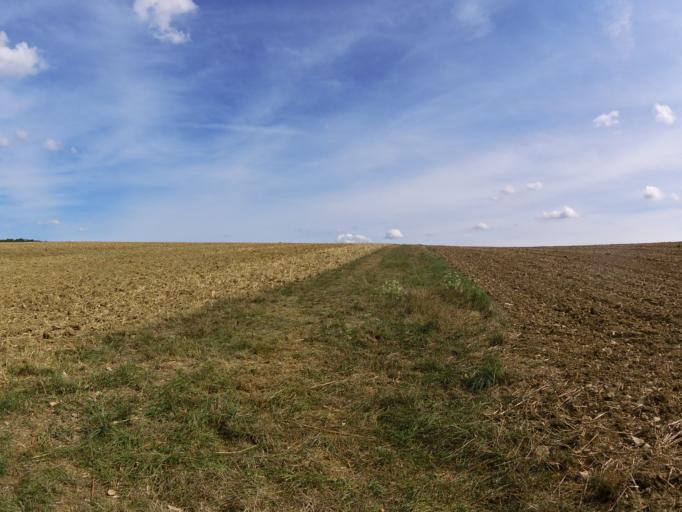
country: DE
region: Bavaria
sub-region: Regierungsbezirk Unterfranken
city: Guntersleben
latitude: 49.8614
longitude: 9.9270
